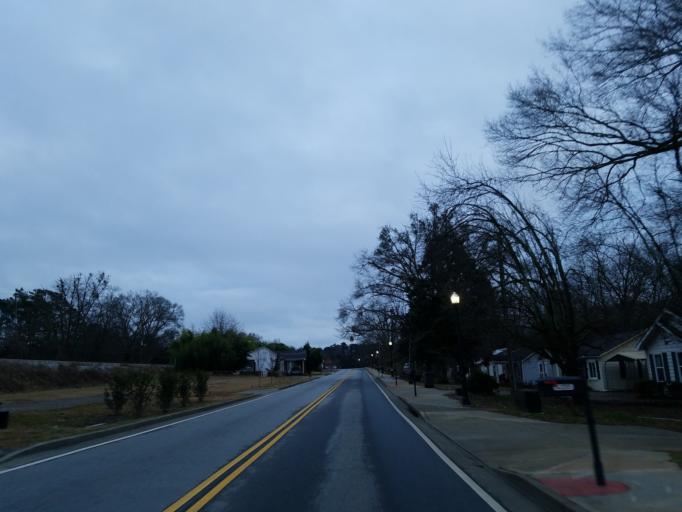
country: US
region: Georgia
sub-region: Cobb County
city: Acworth
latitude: 34.0732
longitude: -84.6893
